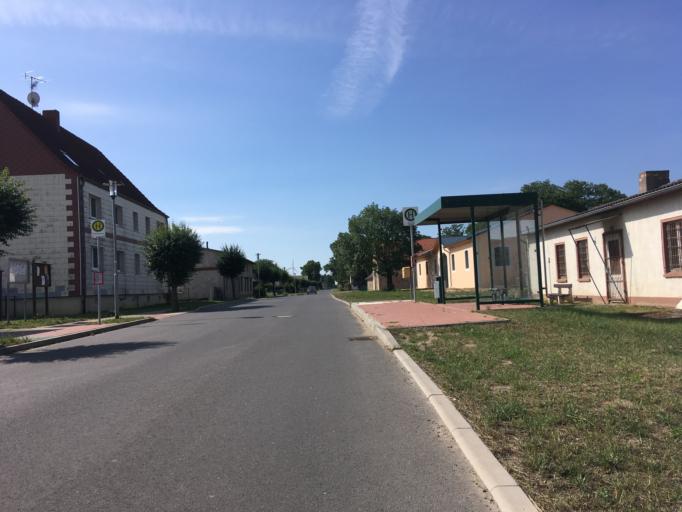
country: DE
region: Brandenburg
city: Grunow
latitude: 53.3009
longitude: 14.0409
